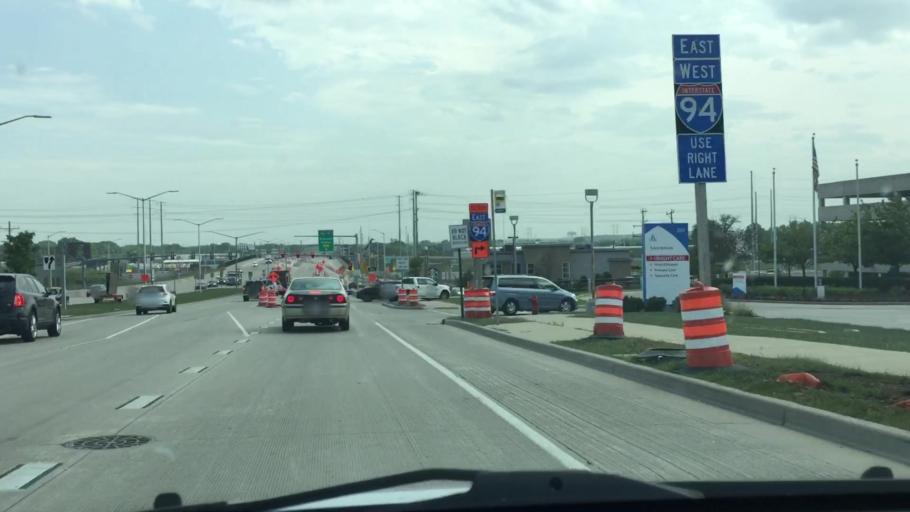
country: US
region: Wisconsin
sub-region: Waukesha County
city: Elm Grove
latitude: 43.0327
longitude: -88.0474
